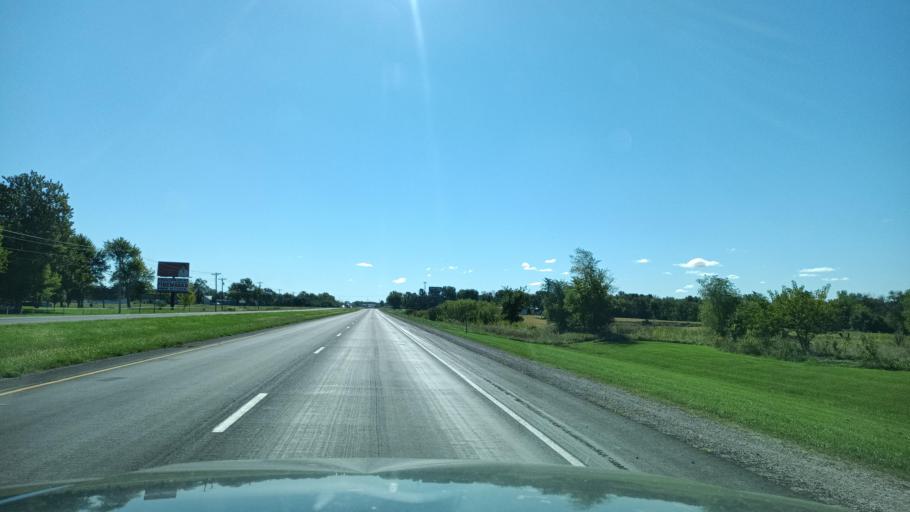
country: US
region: Iowa
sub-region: Lee County
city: Keokuk
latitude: 40.4438
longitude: -91.4379
